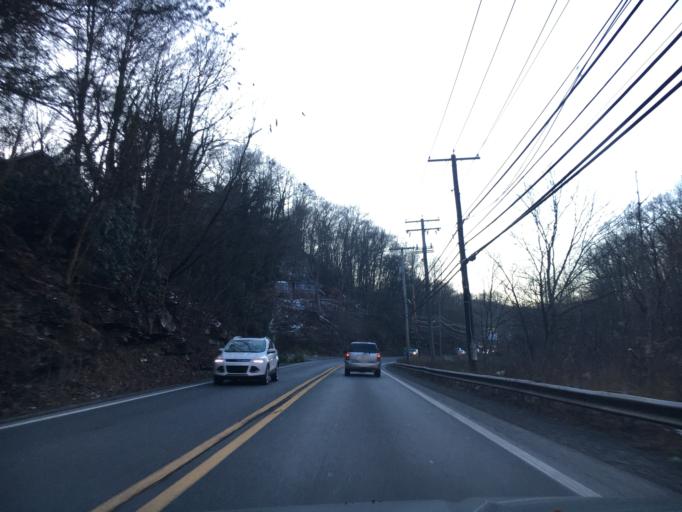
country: US
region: West Virginia
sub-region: Raleigh County
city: Beaver
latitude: 37.7557
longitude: -81.1527
